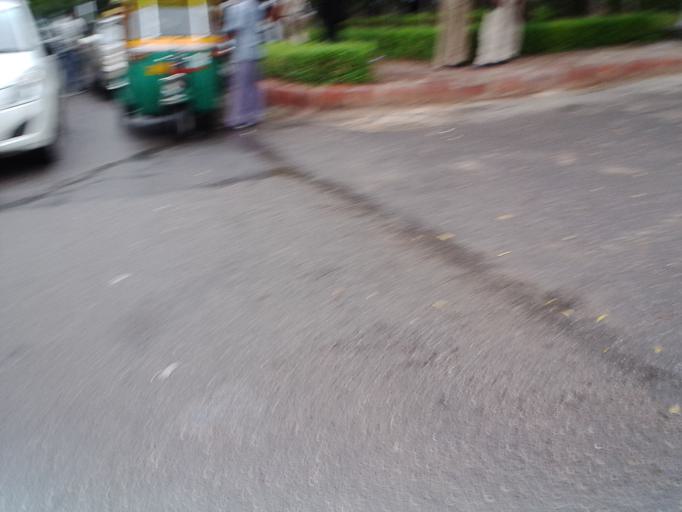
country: IN
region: NCT
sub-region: New Delhi
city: New Delhi
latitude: 28.6096
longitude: 77.2369
